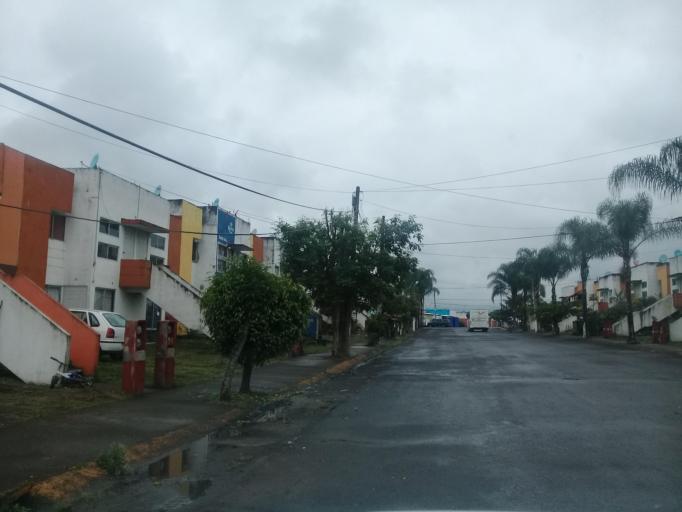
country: MX
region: Veracruz
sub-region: Amatlan de los Reyes
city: Trapiche Viejo
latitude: 18.8377
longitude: -96.9517
